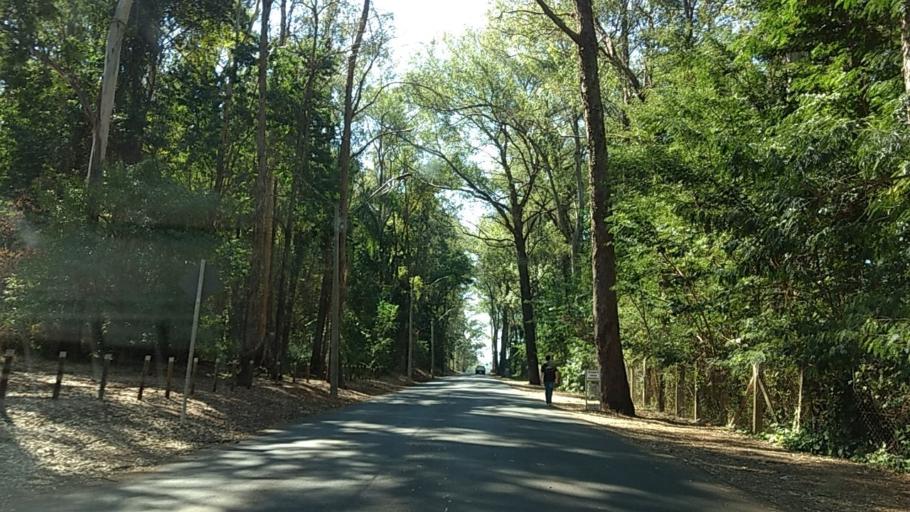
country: BR
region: Sao Paulo
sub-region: Botucatu
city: Botucatu
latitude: -22.8555
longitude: -48.4319
